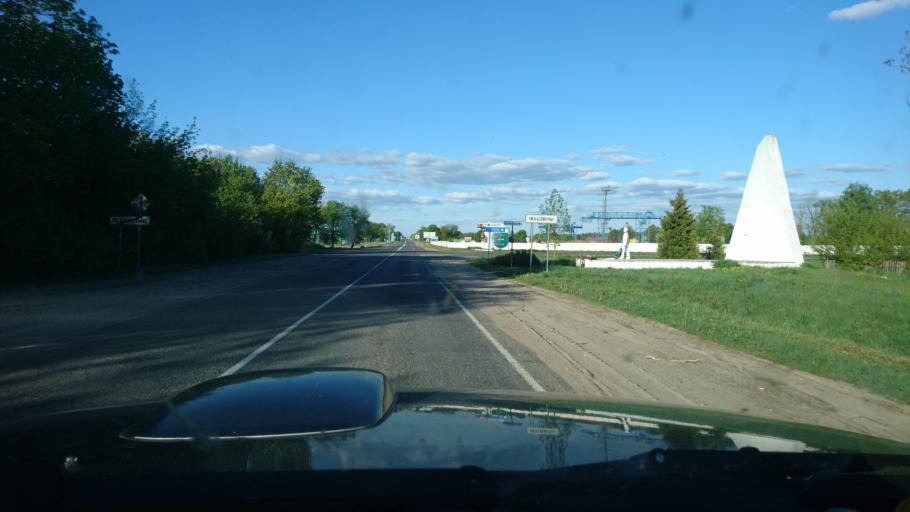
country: BY
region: Brest
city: Ivatsevichy
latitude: 52.6986
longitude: 25.3161
